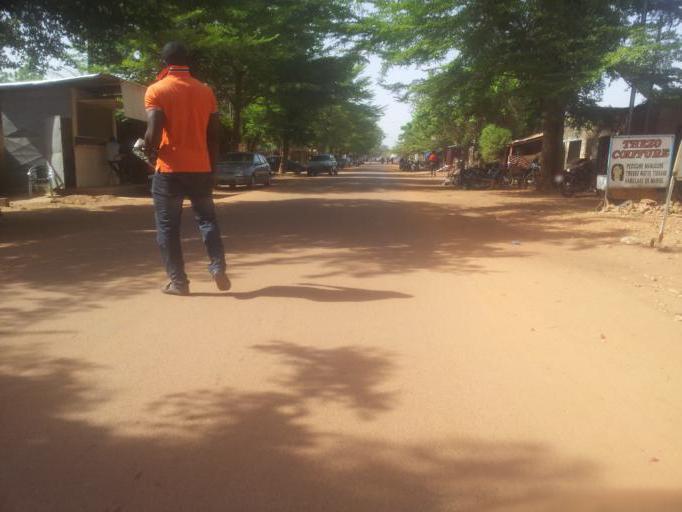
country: BF
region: Centre
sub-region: Kadiogo Province
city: Ouagadougou
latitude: 12.3782
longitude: -1.5371
